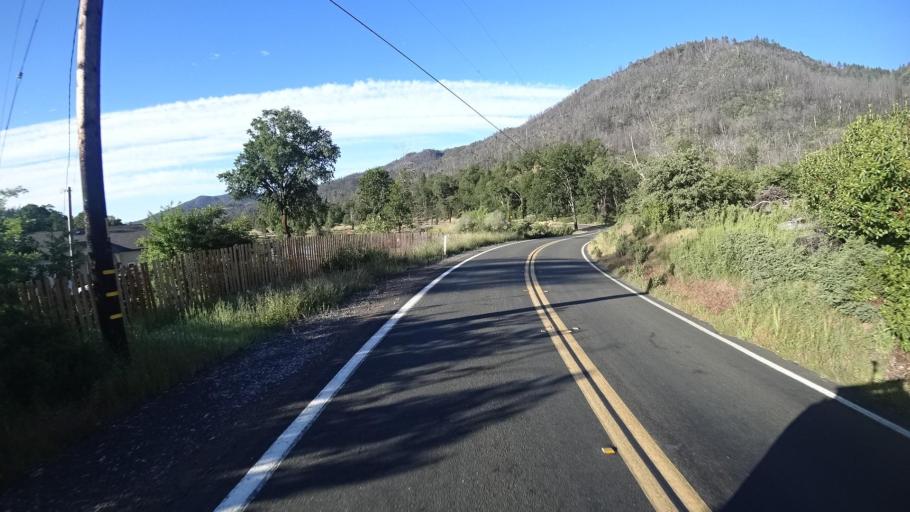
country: US
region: California
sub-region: Lake County
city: Upper Lake
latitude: 39.2356
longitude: -122.9454
